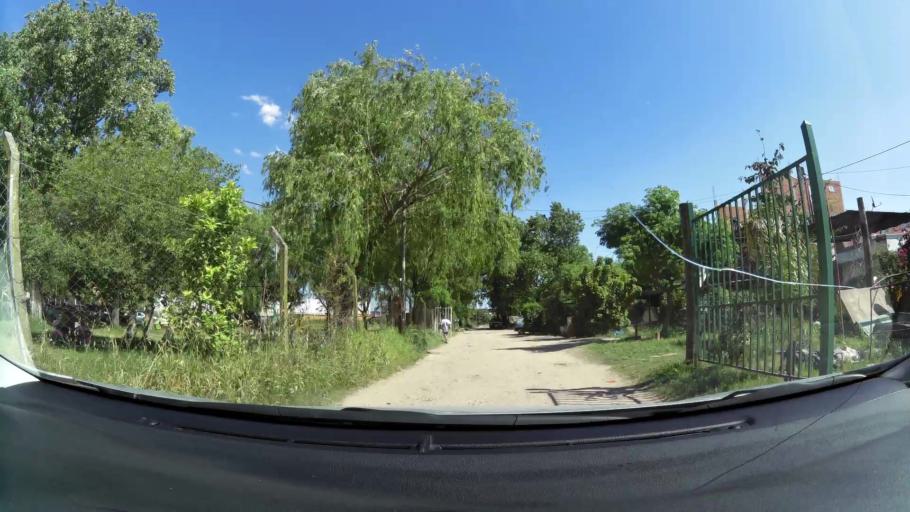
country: AR
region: Buenos Aires F.D.
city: Villa Lugano
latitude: -34.7029
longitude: -58.4699
